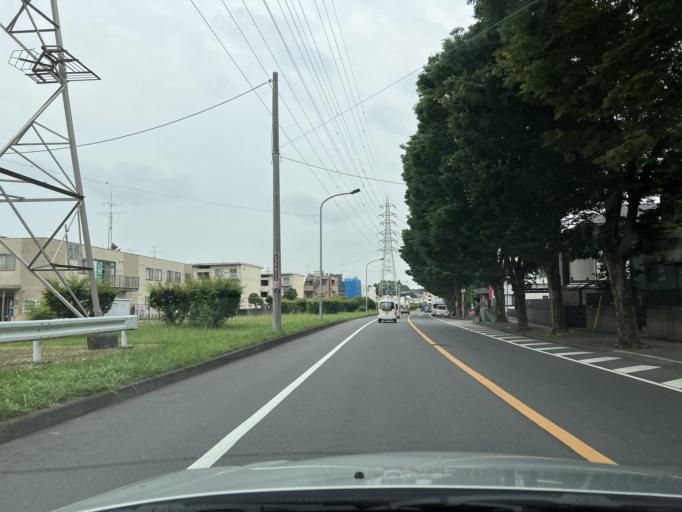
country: JP
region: Chiba
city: Kashiwa
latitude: 35.8145
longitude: 139.9391
